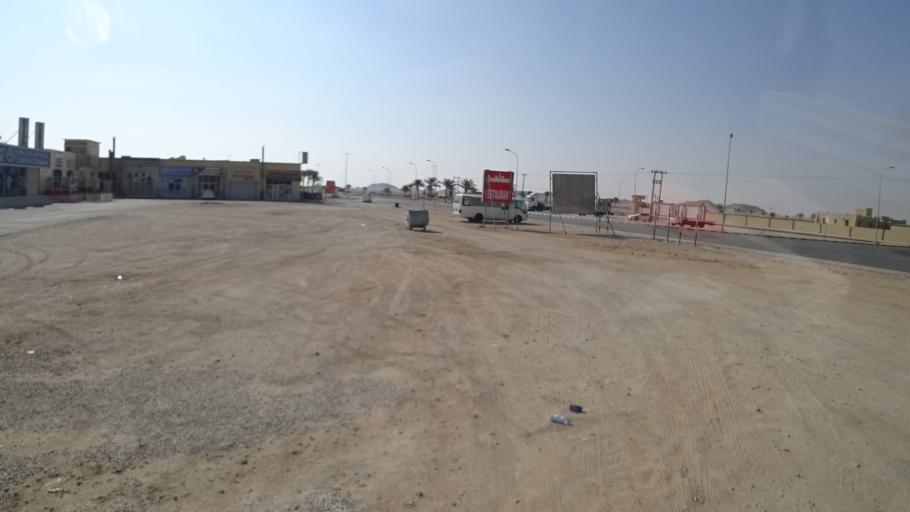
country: OM
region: Zufar
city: Salalah
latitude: 17.6130
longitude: 54.0353
